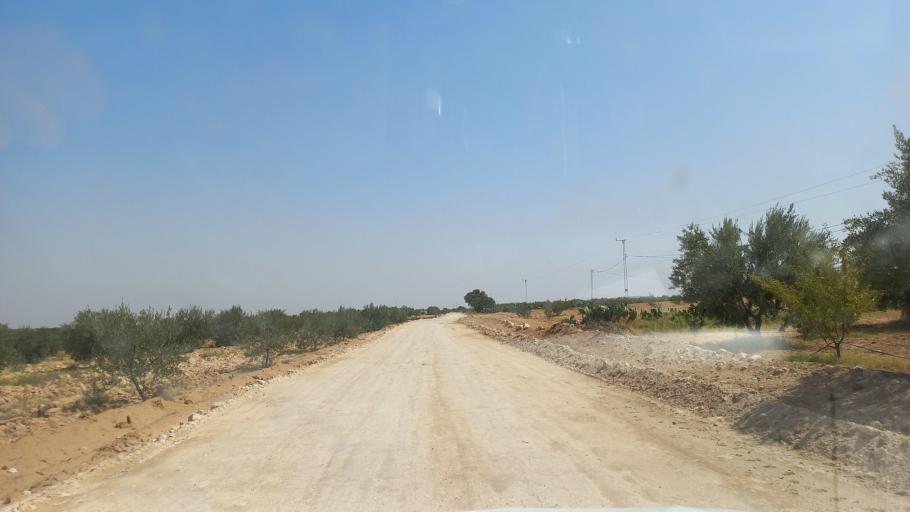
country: TN
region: Al Qasrayn
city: Kasserine
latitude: 35.2629
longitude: 9.0088
